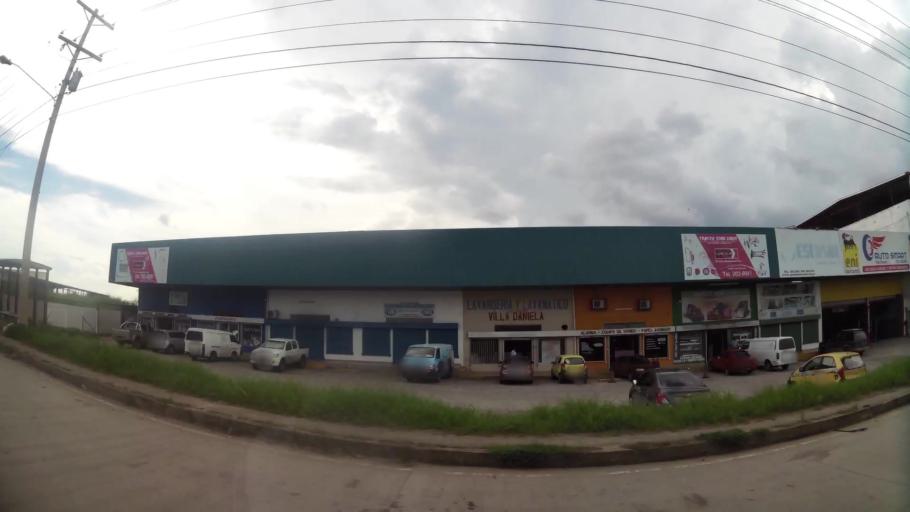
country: PA
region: Panama
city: Tocumen
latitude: 9.0932
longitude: -79.3946
